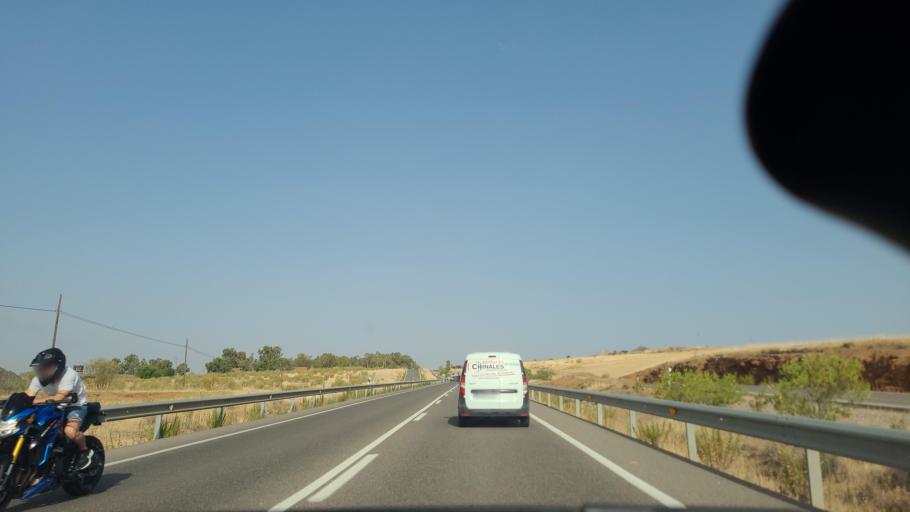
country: ES
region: Andalusia
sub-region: Province of Cordoba
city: Penarroya-Pueblonuevo
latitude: 38.2951
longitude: -5.2370
